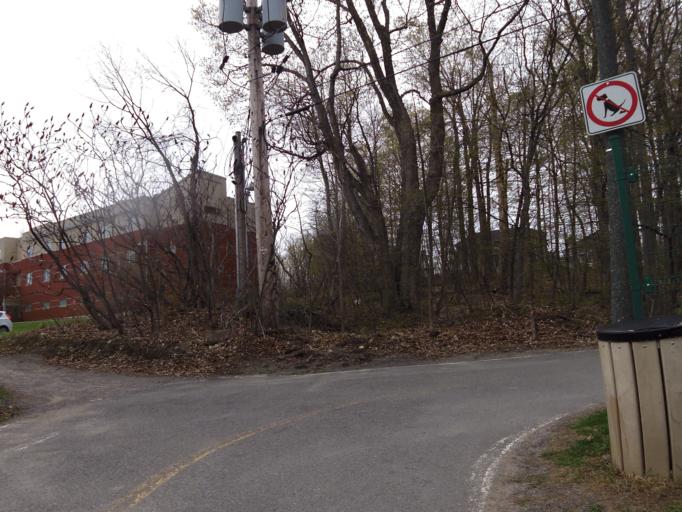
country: CA
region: Quebec
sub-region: Laurentides
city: Deux-Montagnes
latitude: 45.5428
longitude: -73.9157
